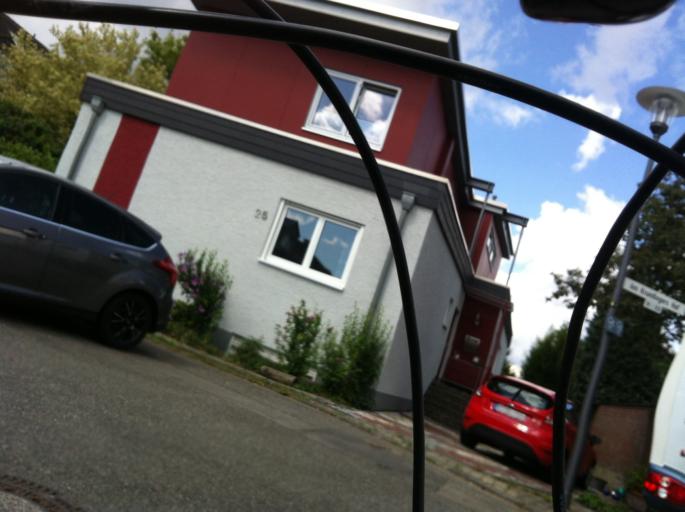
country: DE
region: North Rhine-Westphalia
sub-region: Regierungsbezirk Koln
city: Poll
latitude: 50.8969
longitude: 7.0205
